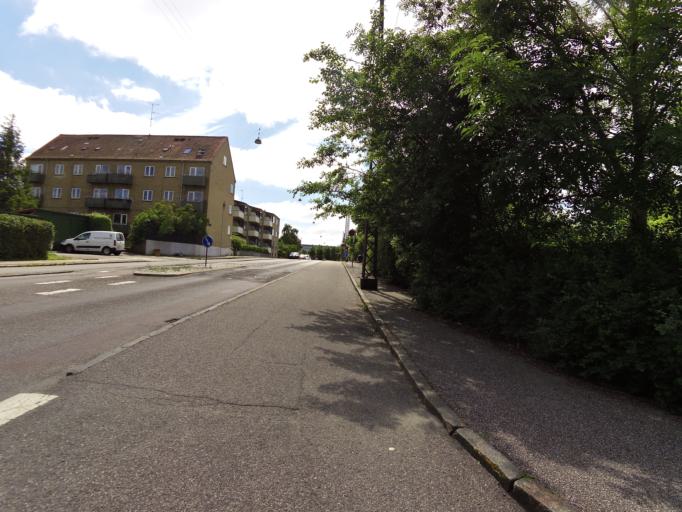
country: DK
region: Capital Region
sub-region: Frederiksberg Kommune
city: Frederiksberg
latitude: 55.7126
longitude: 12.5167
